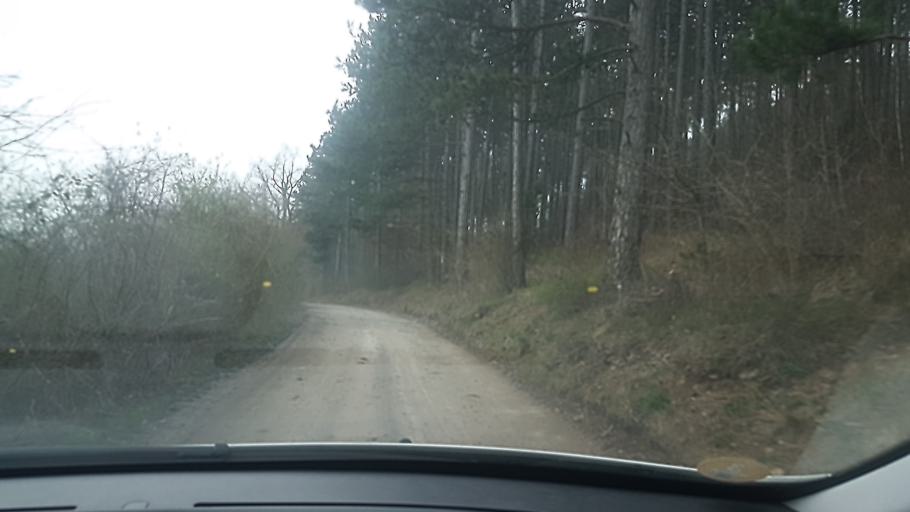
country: BE
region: Wallonia
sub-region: Province de Namur
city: Couvin
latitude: 50.0758
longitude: 4.5902
